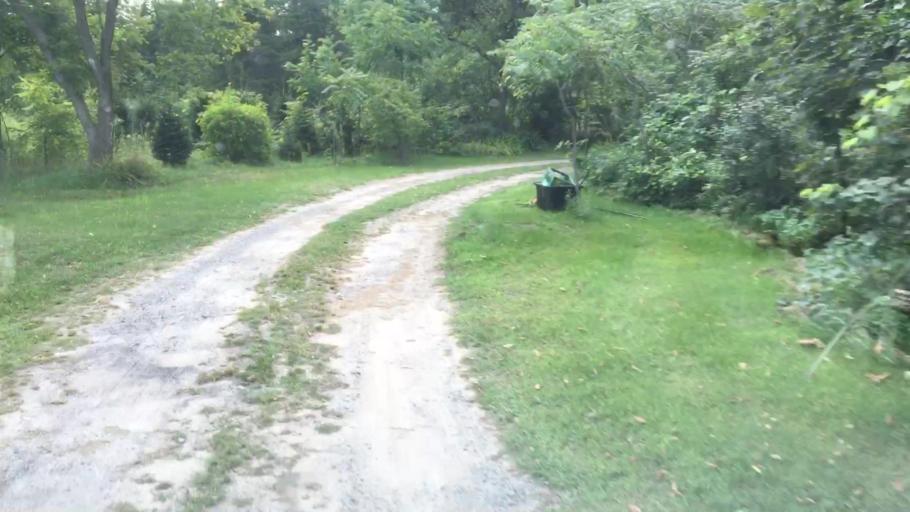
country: CA
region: Ontario
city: Quinte West
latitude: 44.0277
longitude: -77.7811
